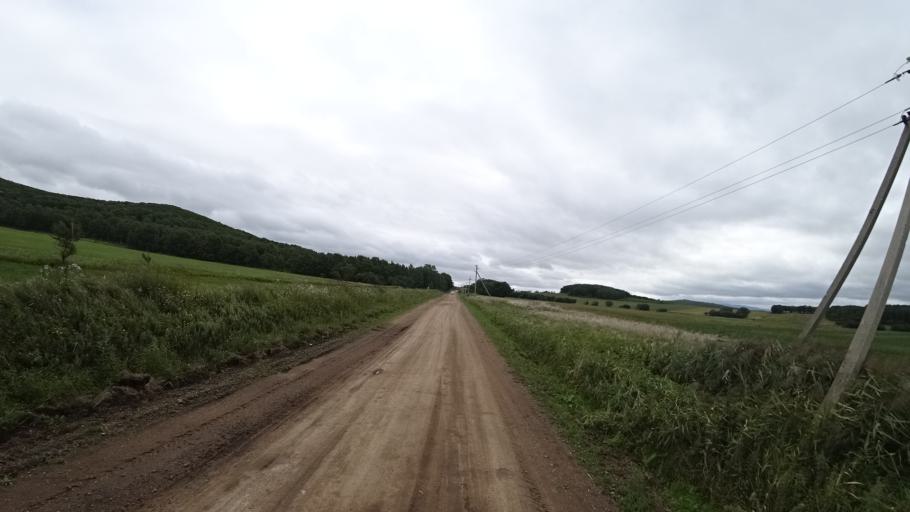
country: RU
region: Primorskiy
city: Chernigovka
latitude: 44.4705
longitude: 132.5822
